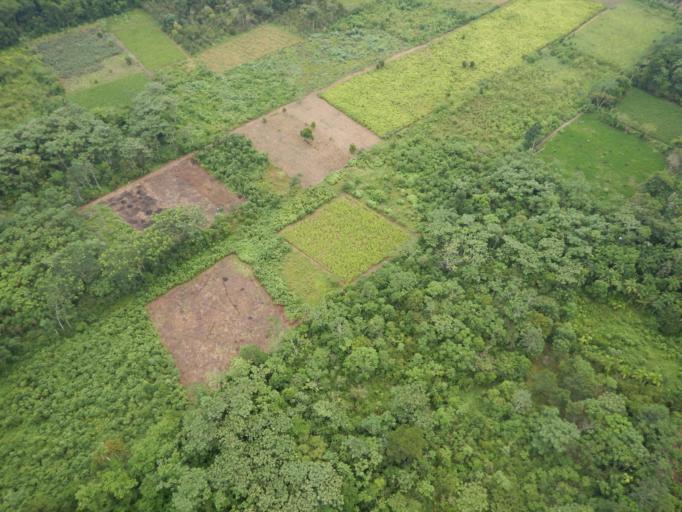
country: BO
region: Cochabamba
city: Chimore
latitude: -17.2298
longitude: -64.6933
